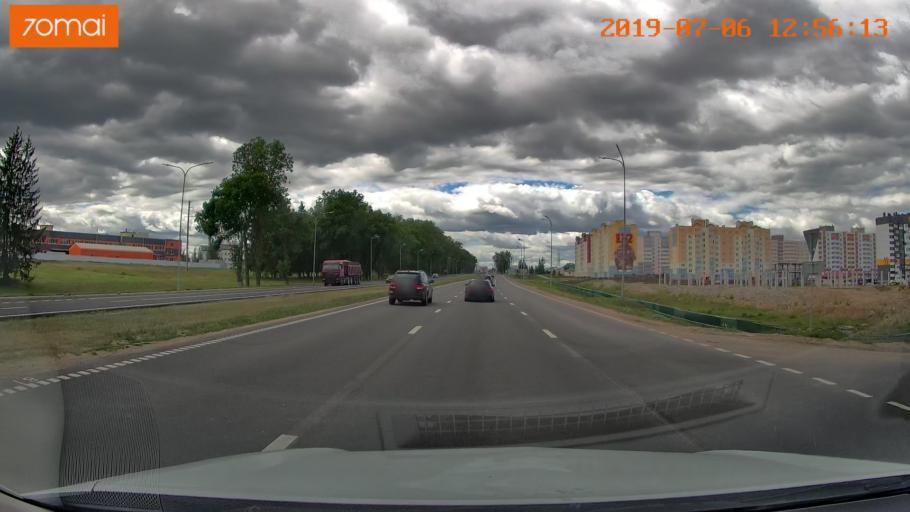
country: BY
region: Minsk
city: Dzyarzhynsk
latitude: 53.6900
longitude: 27.1636
